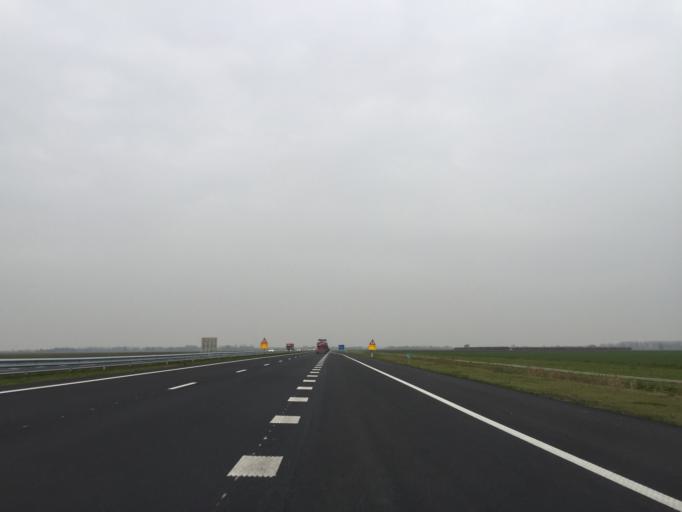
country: NL
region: North Brabant
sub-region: Gemeente Steenbergen
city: Dinteloord
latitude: 51.6228
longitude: 4.3804
